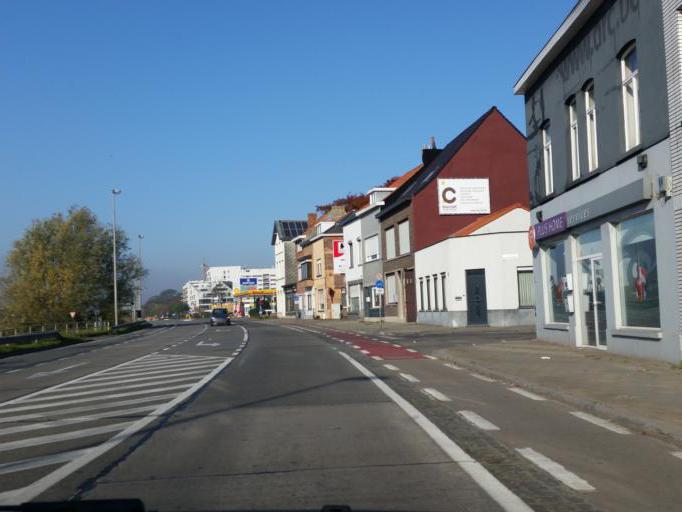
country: BE
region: Flanders
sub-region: Provincie Oost-Vlaanderen
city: Gent
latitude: 51.0674
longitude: 3.6985
